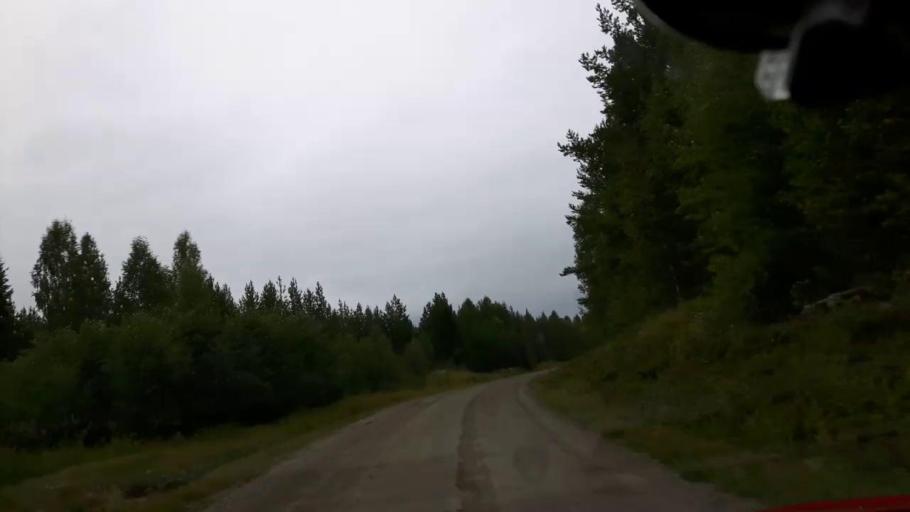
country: SE
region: Vaesternorrland
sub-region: Ange Kommun
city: Fransta
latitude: 62.8552
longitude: 15.9774
